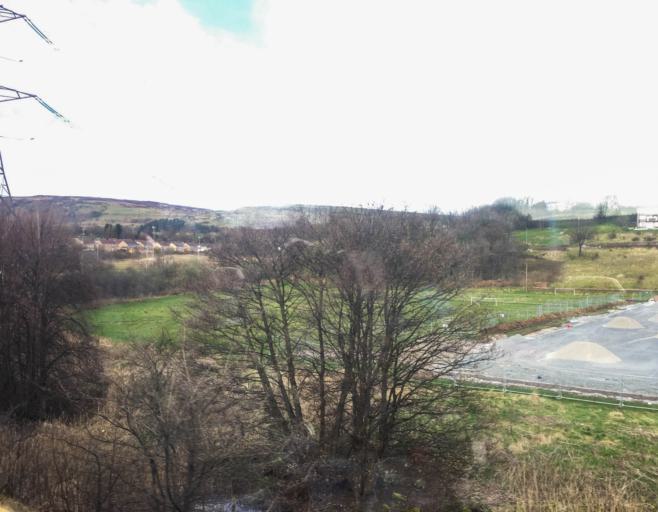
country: GB
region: Scotland
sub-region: West Dunbartonshire
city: Old Kilpatrick
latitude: 55.9174
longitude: -4.4395
